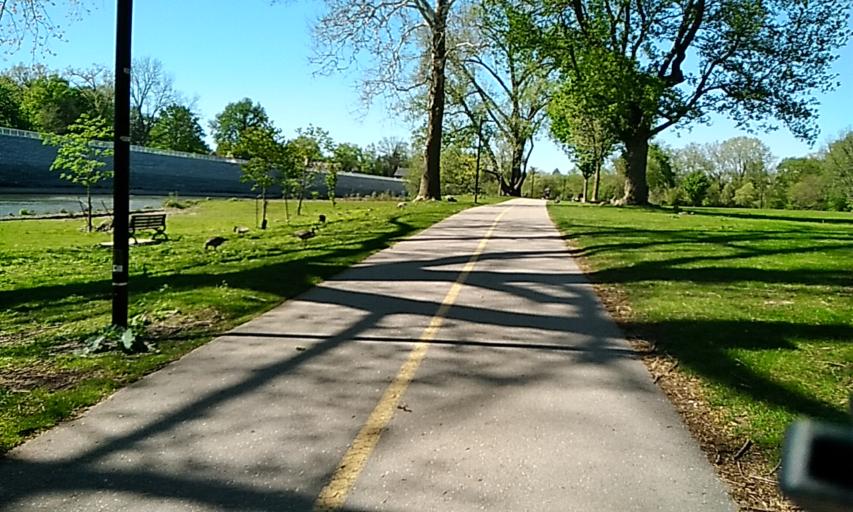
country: CA
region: Ontario
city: London
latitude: 42.9849
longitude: -81.2573
